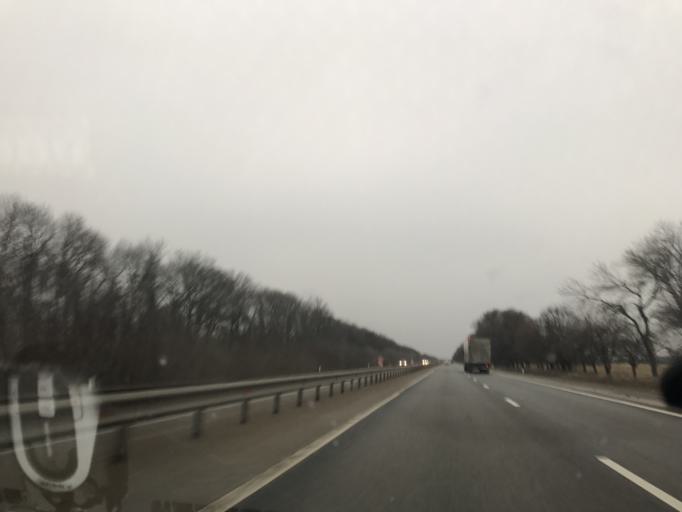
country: RU
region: Krasnodarskiy
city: Pavlovskaya
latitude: 46.1926
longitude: 39.8315
